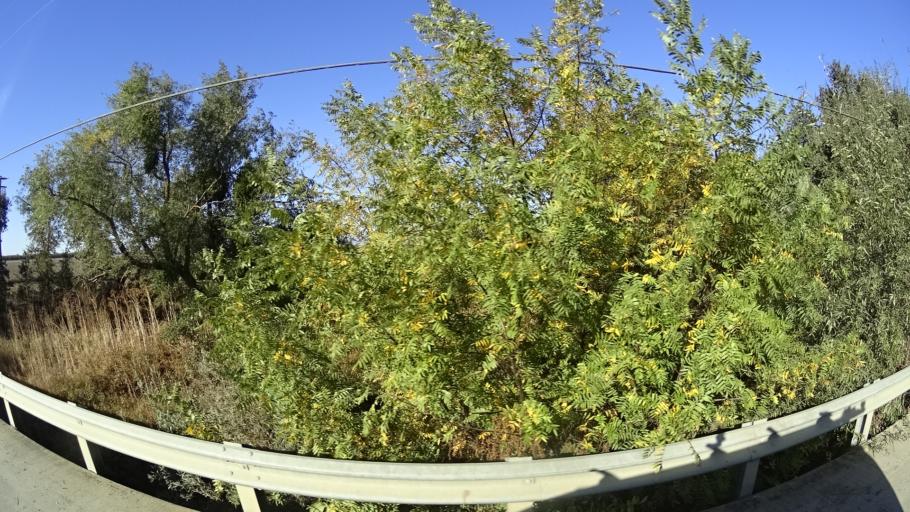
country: US
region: California
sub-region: Yolo County
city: Woodland
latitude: 38.6050
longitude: -121.7854
